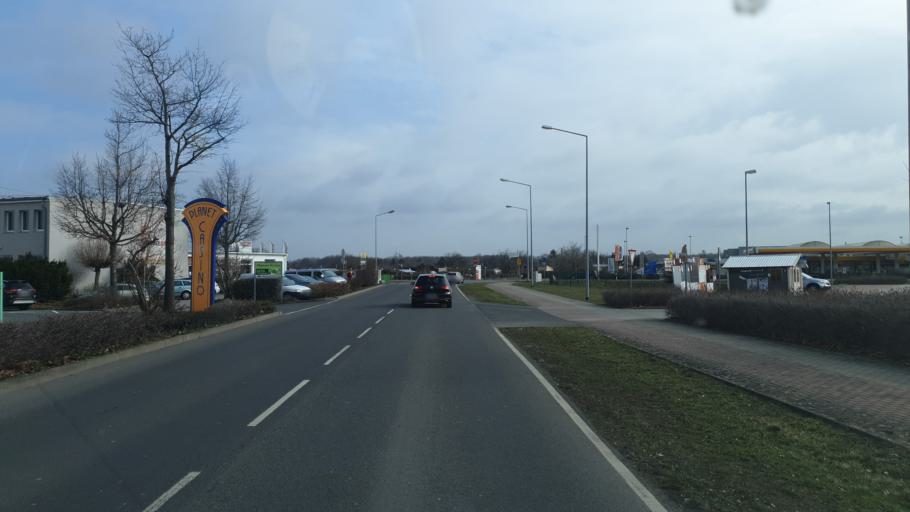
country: DE
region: Saxony
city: Dobernitz
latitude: 51.5124
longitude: 12.3352
